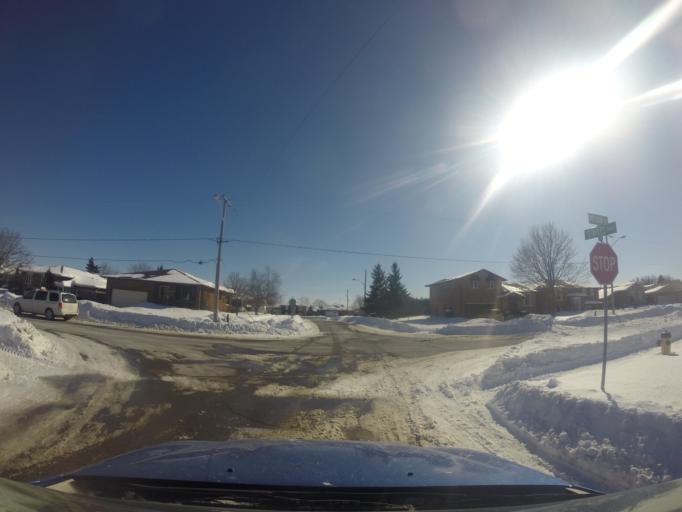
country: CA
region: Ontario
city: Omemee
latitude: 44.3412
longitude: -78.7497
